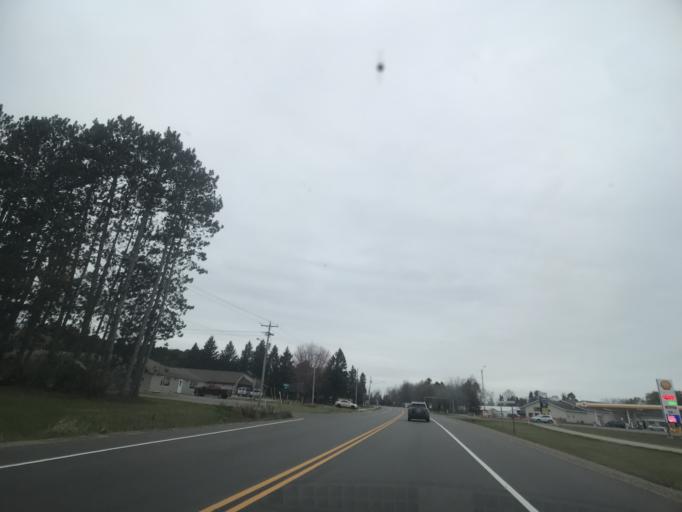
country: US
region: Wisconsin
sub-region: Menominee County
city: Legend Lake
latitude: 45.2983
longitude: -88.5175
